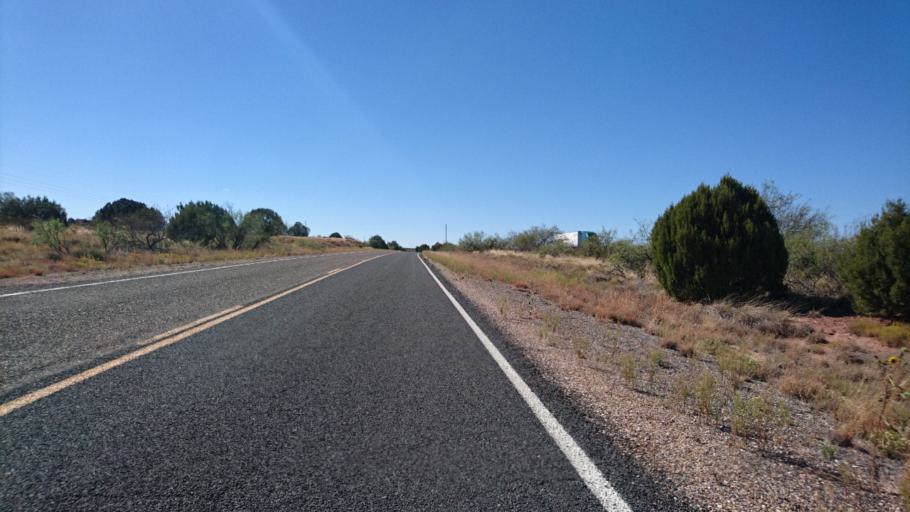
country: US
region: New Mexico
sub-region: Quay County
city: Tucumcari
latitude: 35.0682
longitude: -104.1703
